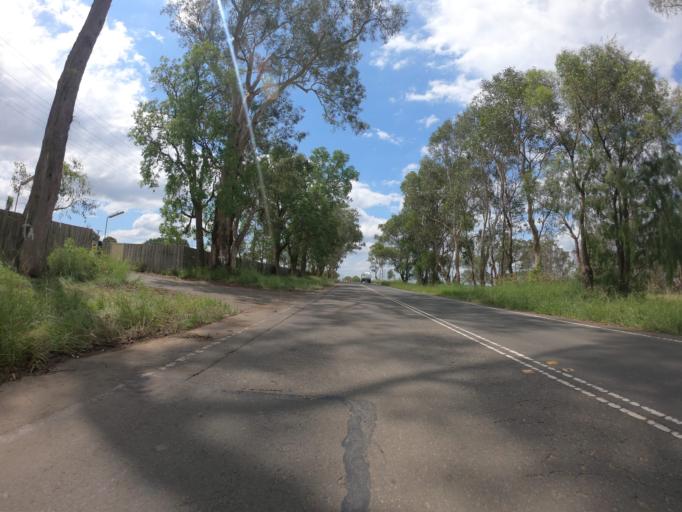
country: AU
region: New South Wales
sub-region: Penrith Municipality
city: Kingswood Park
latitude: -33.8265
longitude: 150.7598
